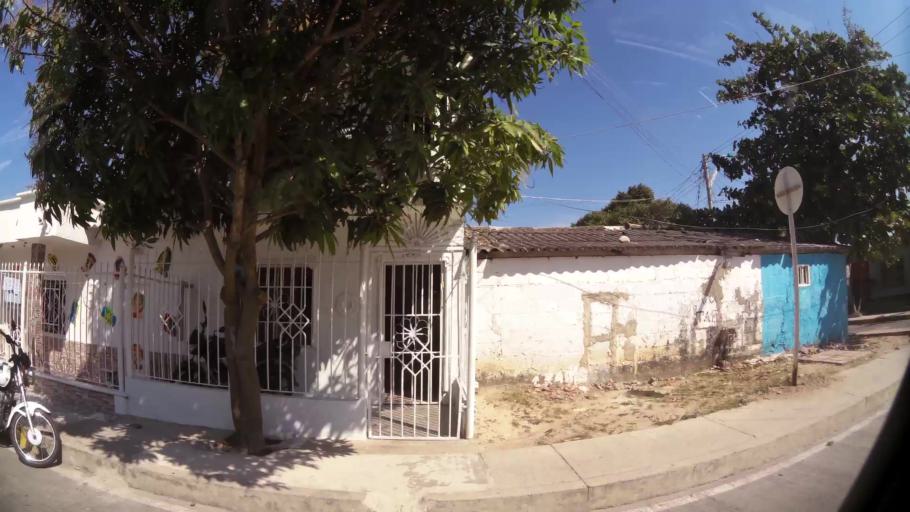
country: CO
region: Atlantico
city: Barranquilla
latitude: 10.9385
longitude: -74.8248
